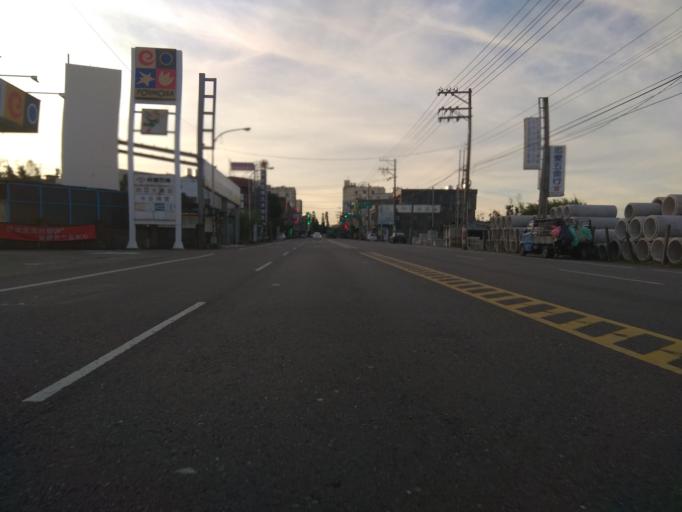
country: TW
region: Taiwan
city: Taoyuan City
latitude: 24.9930
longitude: 121.1697
